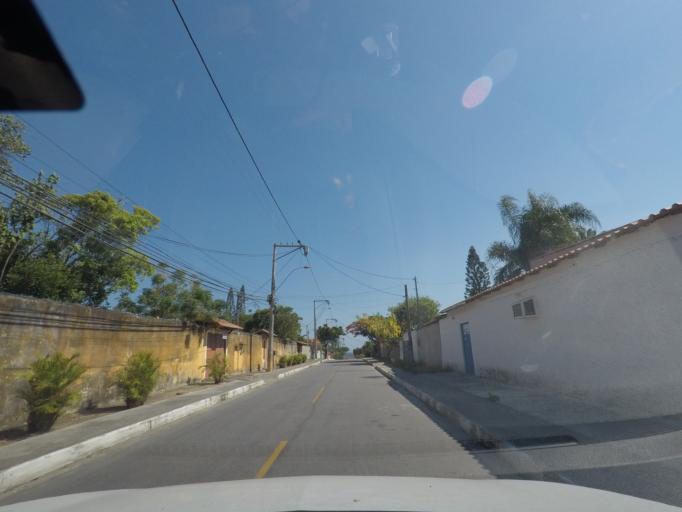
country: BR
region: Rio de Janeiro
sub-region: Niteroi
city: Niteroi
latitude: -22.9649
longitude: -42.9720
